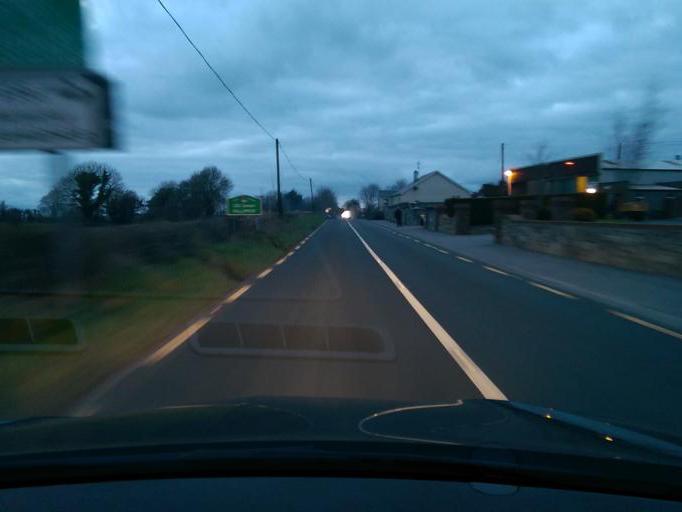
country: IE
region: Connaught
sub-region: County Galway
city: Portumna
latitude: 53.1619
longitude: -8.2796
